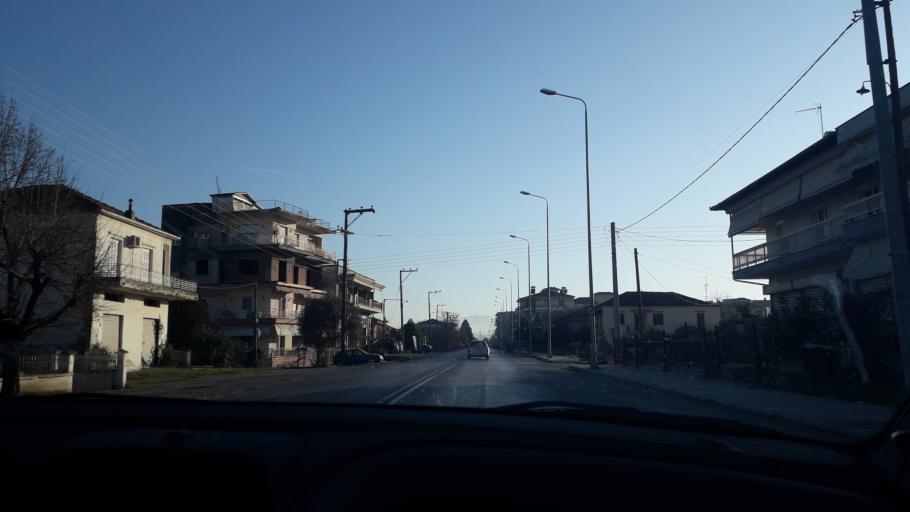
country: GR
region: Central Macedonia
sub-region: Nomos Imathias
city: Alexandreia
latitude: 40.6275
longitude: 22.4484
